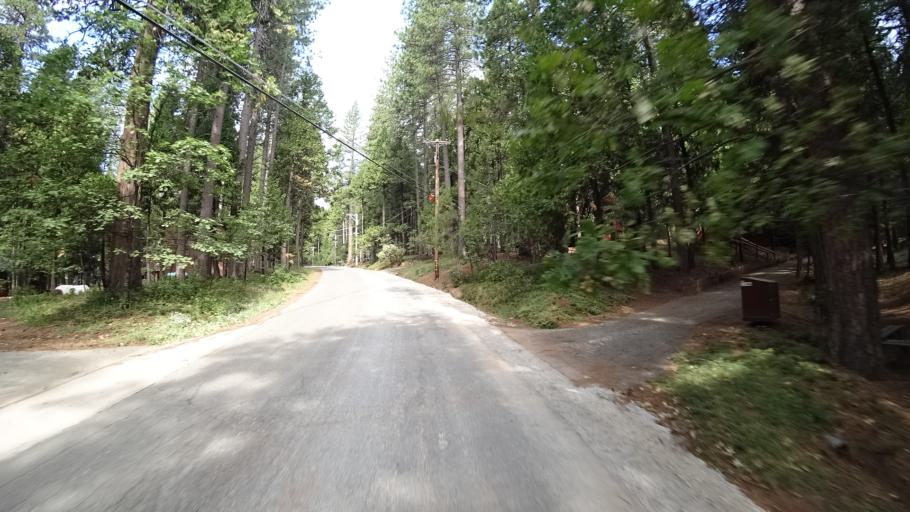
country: US
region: California
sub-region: Calaveras County
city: Arnold
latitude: 38.2532
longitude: -120.3358
